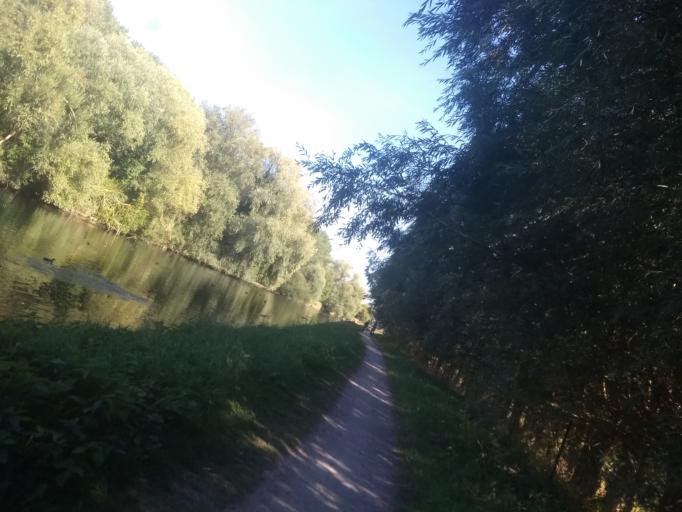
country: FR
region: Nord-Pas-de-Calais
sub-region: Departement du Pas-de-Calais
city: Feuchy
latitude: 50.2971
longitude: 2.8444
